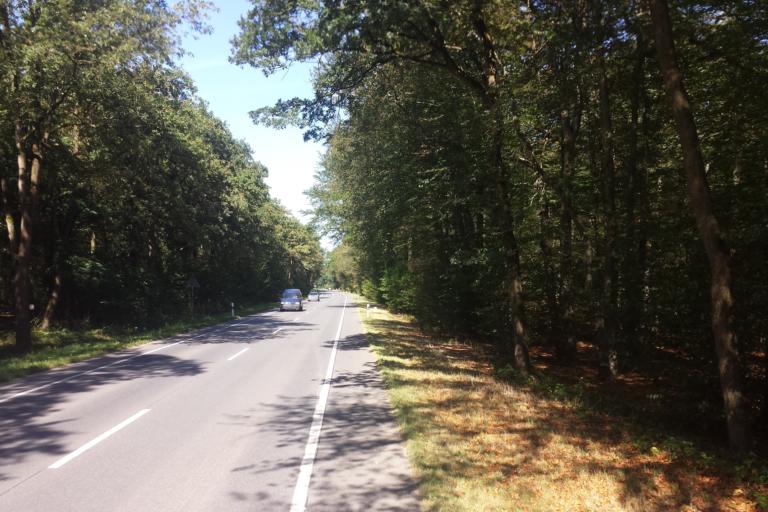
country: DE
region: Hesse
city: Viernheim
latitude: 49.5838
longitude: 8.5899
